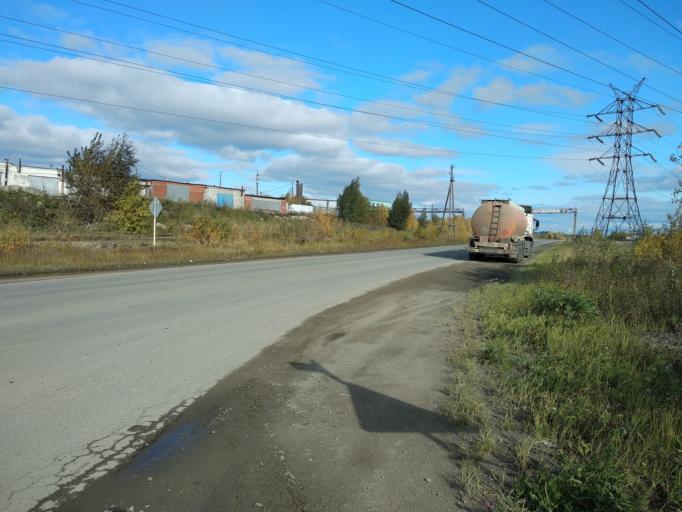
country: RU
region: Sverdlovsk
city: Krasnotur'insk
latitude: 59.7775
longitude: 60.1969
